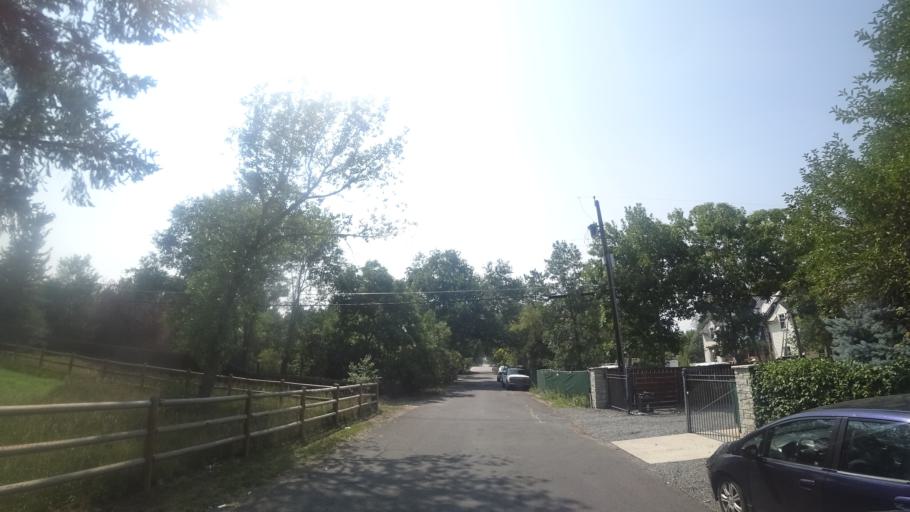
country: US
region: Colorado
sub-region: Arapahoe County
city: Englewood
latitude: 39.6368
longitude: -104.9770
